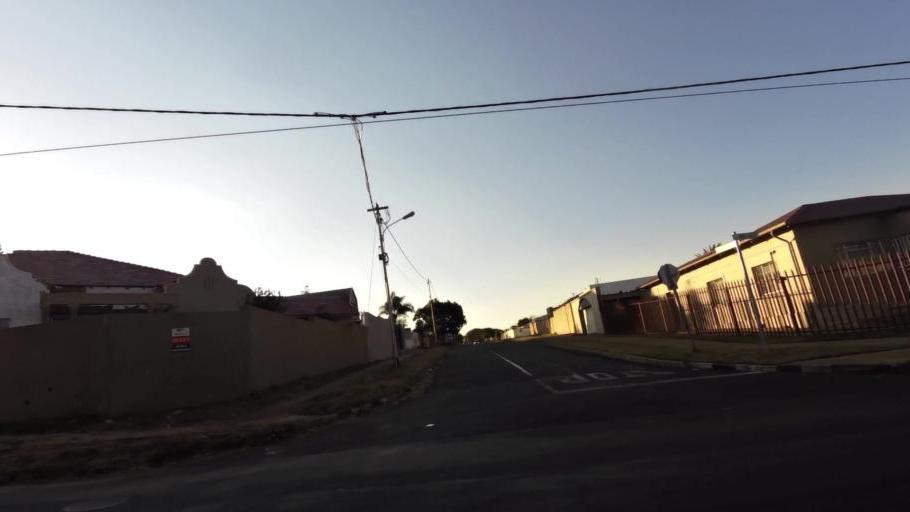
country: ZA
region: Gauteng
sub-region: City of Johannesburg Metropolitan Municipality
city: Roodepoort
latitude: -26.1729
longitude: 27.9510
